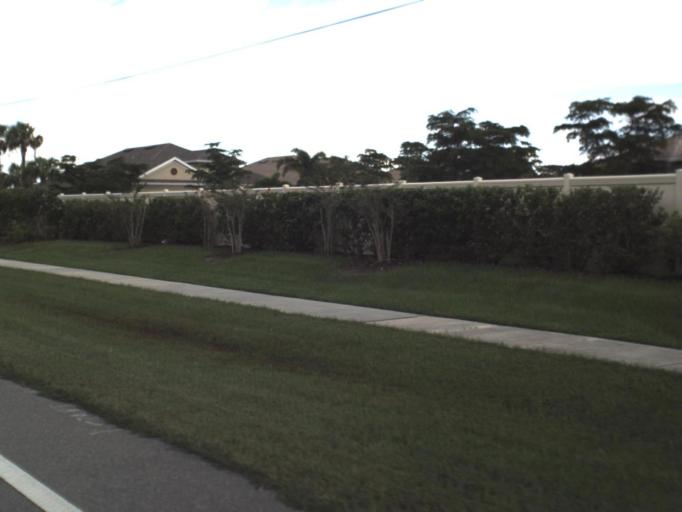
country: US
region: Florida
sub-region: Sarasota County
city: Venice Gardens
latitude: 27.0995
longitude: -82.3916
